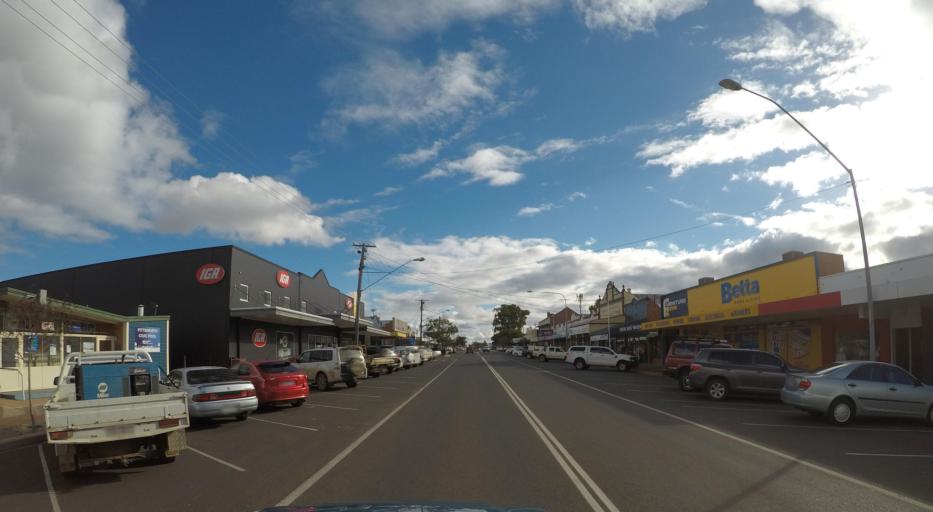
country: AU
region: Queensland
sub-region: Toowoomba
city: Westbrook
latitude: -27.7156
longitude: 151.6359
